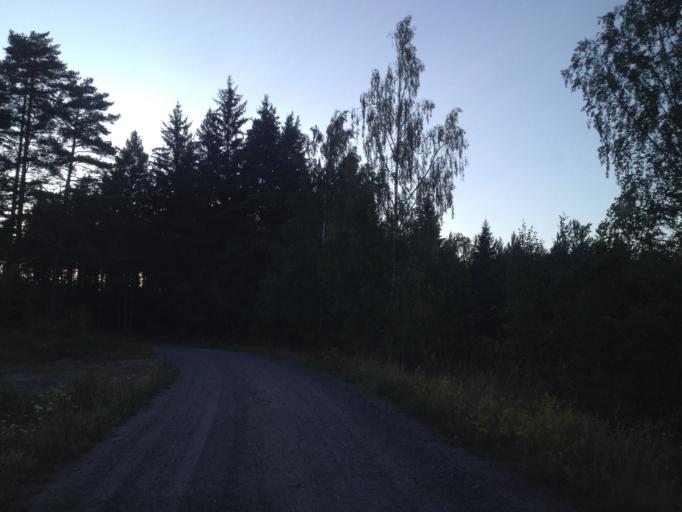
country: SE
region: Kalmar
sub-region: Vasterviks Kommun
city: Overum
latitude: 58.0222
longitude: 16.1179
